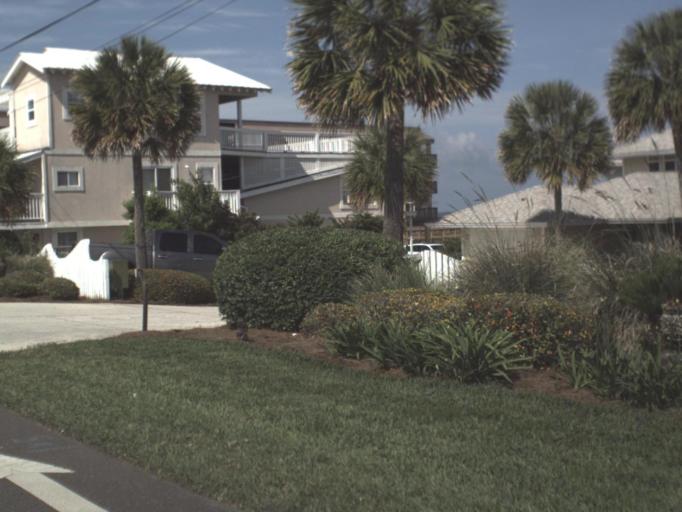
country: US
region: Florida
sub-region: Nassau County
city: Fernandina Beach
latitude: 30.6229
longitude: -81.4404
